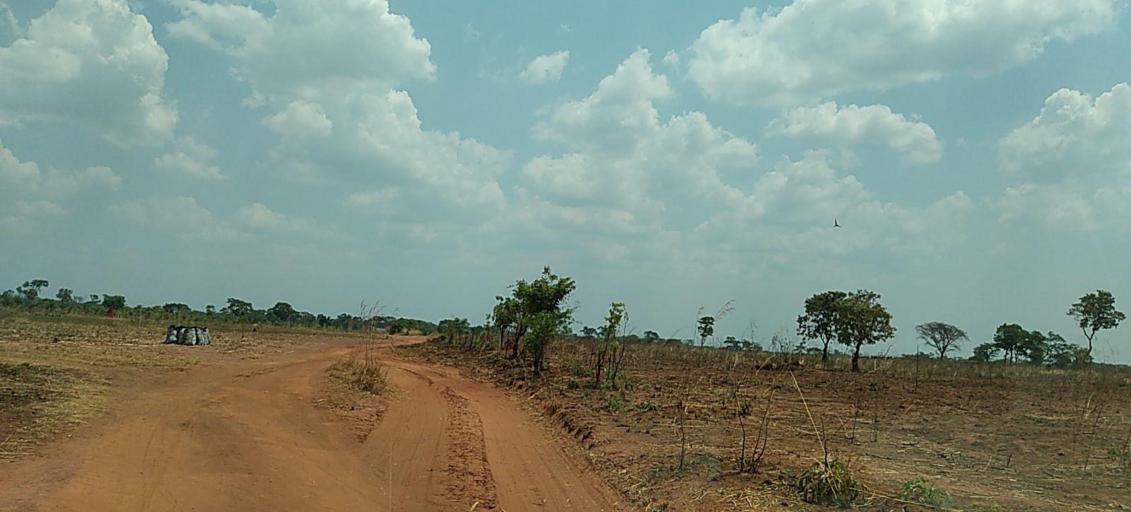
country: ZM
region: Copperbelt
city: Mpongwe
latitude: -13.6605
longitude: 28.0244
